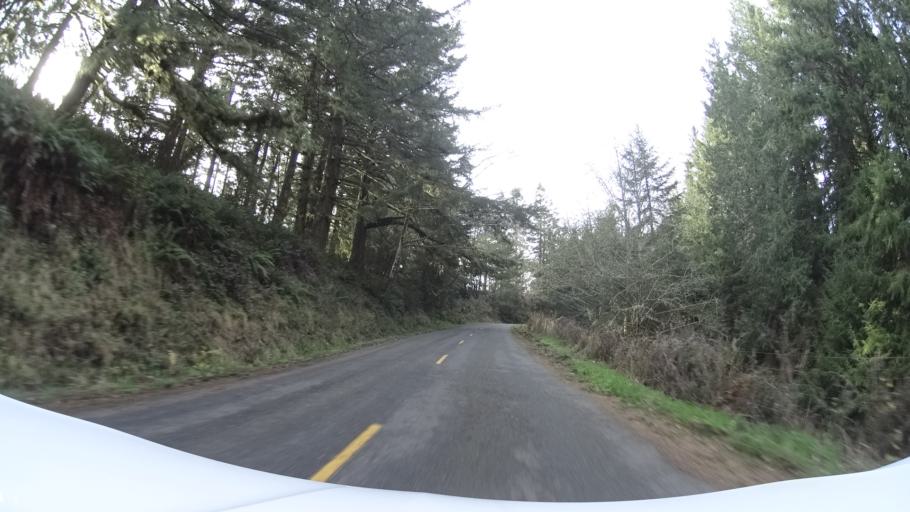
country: US
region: California
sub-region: Humboldt County
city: Ferndale
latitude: 40.5354
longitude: -124.2730
